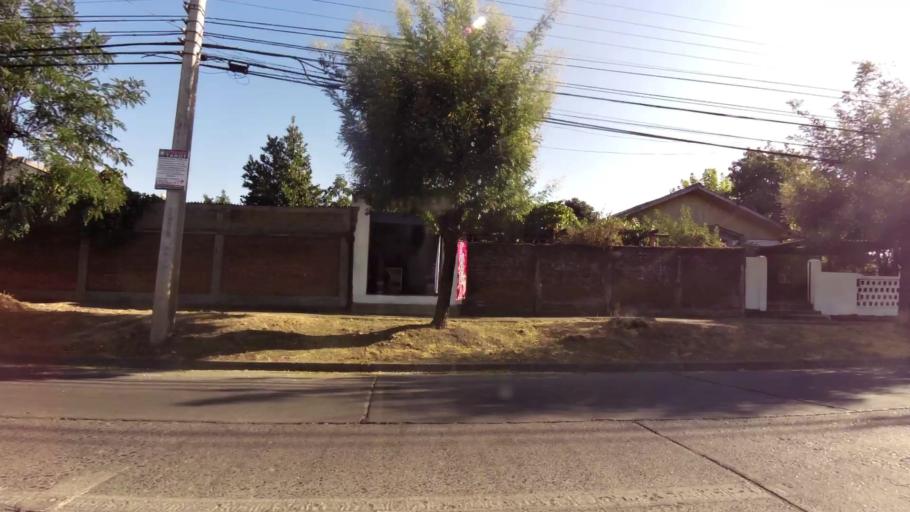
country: CL
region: Maule
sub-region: Provincia de Talca
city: Talca
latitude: -35.4346
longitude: -71.6714
